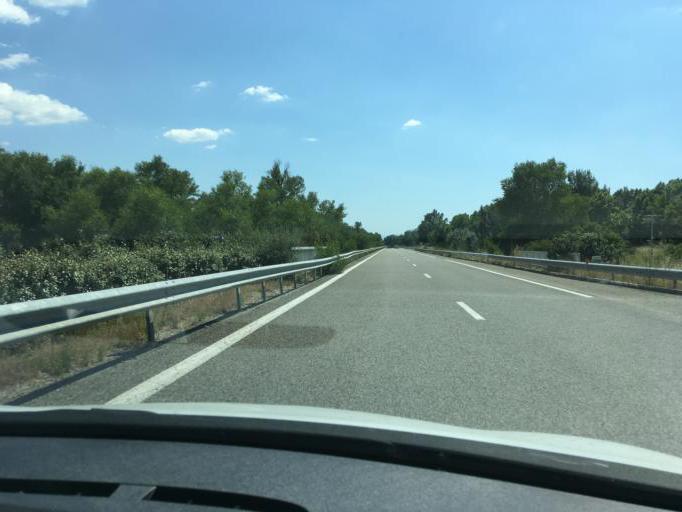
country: FR
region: Provence-Alpes-Cote d'Azur
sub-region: Departement des Alpes-de-Haute-Provence
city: Volx
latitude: 43.8435
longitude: 5.8495
